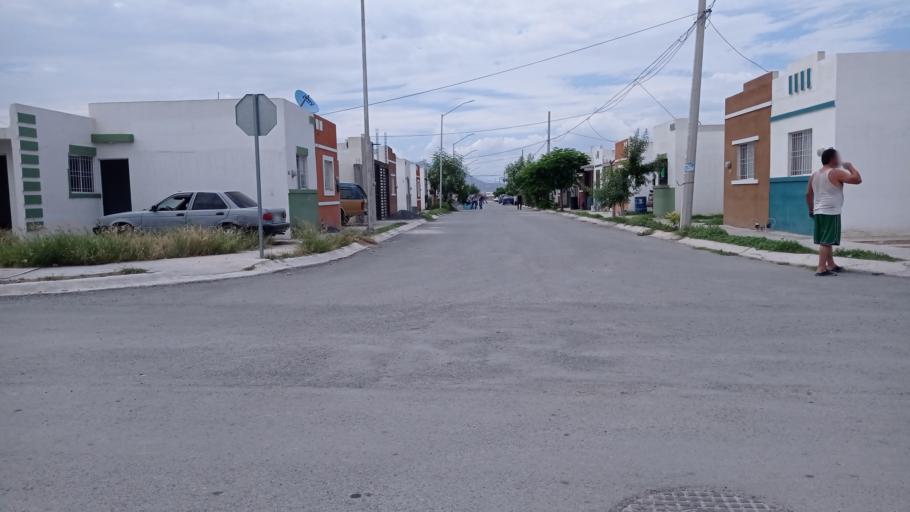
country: MX
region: Nuevo Leon
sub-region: Salinas Victoria
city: Simeprodeso (Colectivo Nuevo)
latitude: 25.8746
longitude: -100.3158
